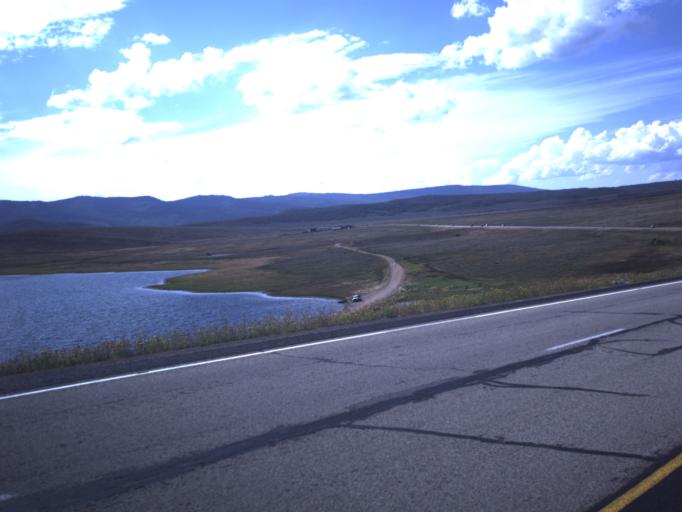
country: US
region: Utah
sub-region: Wasatch County
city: Heber
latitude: 40.2339
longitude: -111.1328
